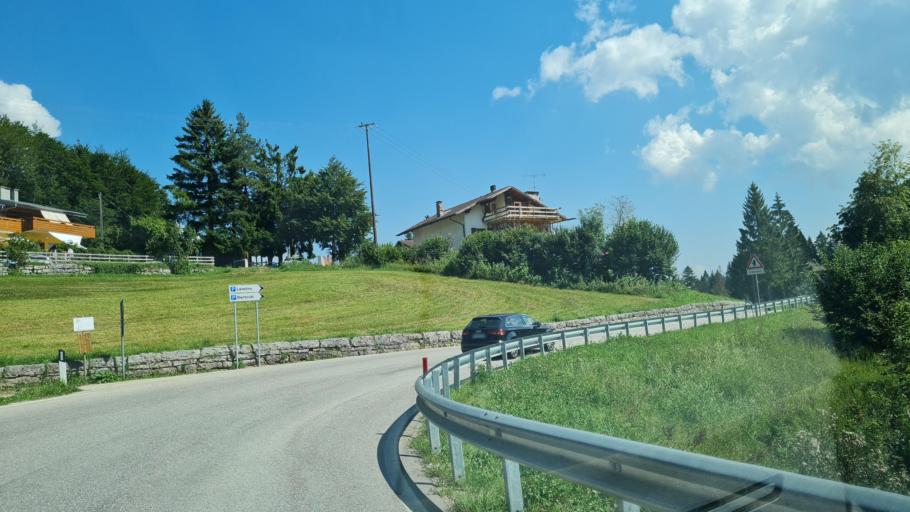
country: IT
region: Trentino-Alto Adige
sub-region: Provincia di Trento
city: Centa San Nicolo
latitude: 45.9475
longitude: 11.2463
